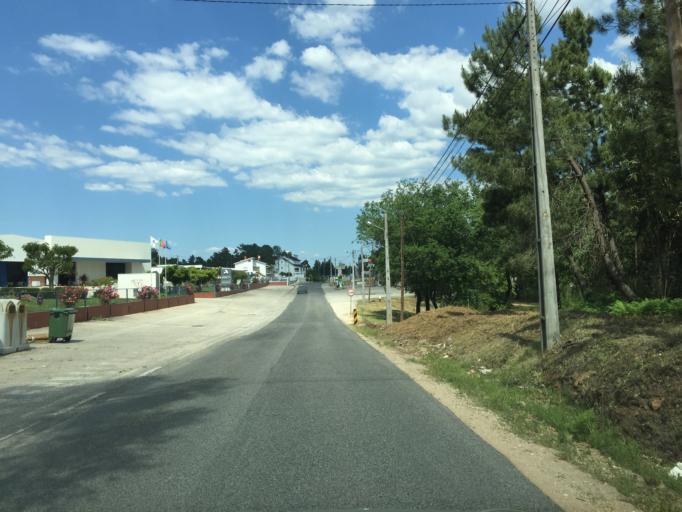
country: PT
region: Santarem
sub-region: Ourem
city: Ourem
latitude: 39.6836
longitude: -8.5631
